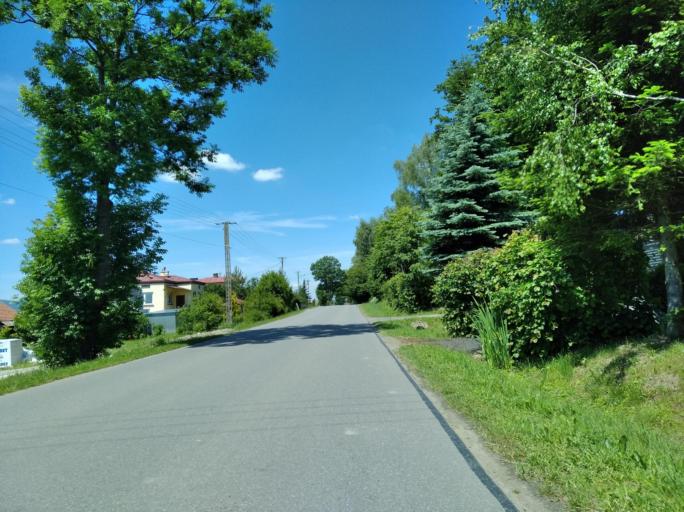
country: PL
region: Subcarpathian Voivodeship
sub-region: Powiat jasielski
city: Nowy Zmigrod
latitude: 49.6171
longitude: 21.5722
